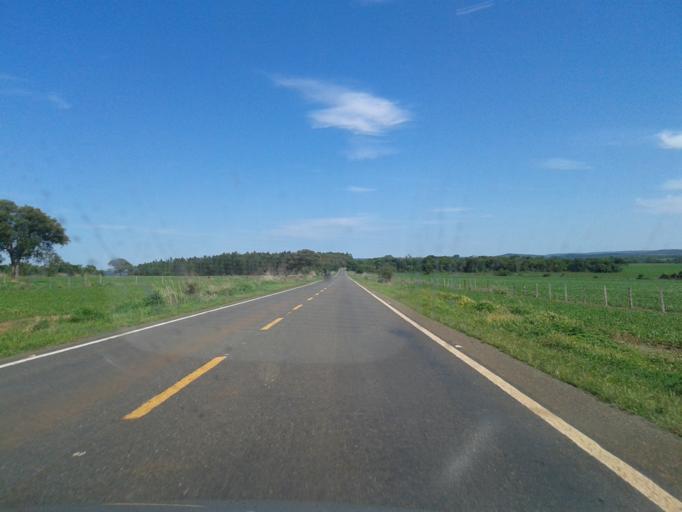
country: BR
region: Goias
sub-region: Piracanjuba
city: Piracanjuba
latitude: -17.3368
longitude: -48.7957
